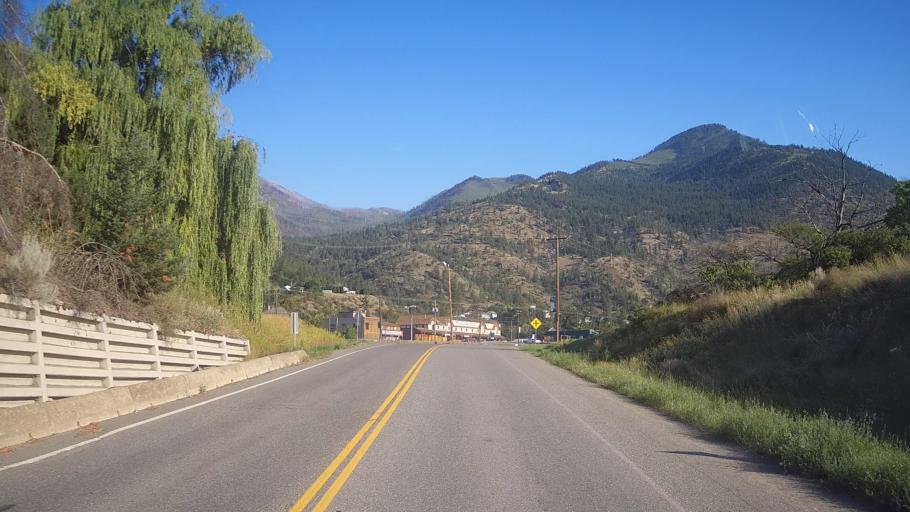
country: CA
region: British Columbia
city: Lillooet
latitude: 50.6844
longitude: -121.9342
